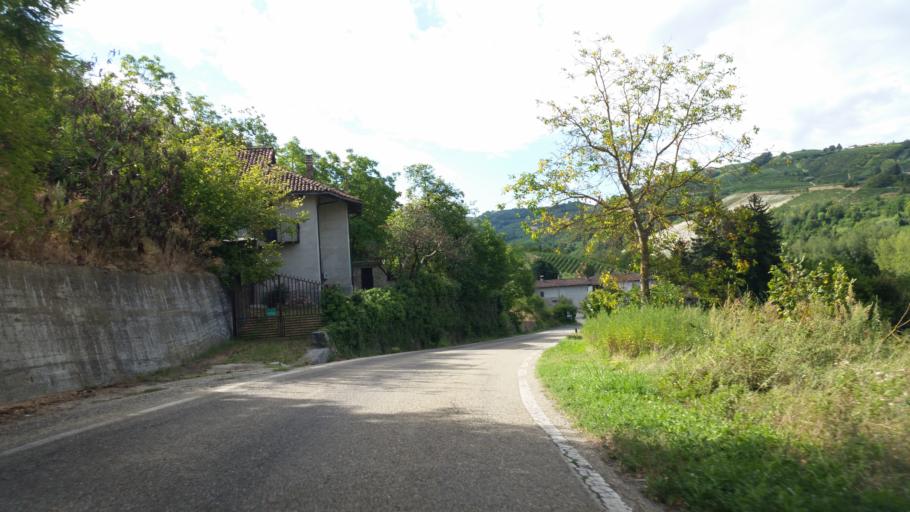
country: IT
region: Piedmont
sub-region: Provincia di Cuneo
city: Bricco di Neive
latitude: 44.7069
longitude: 8.1288
